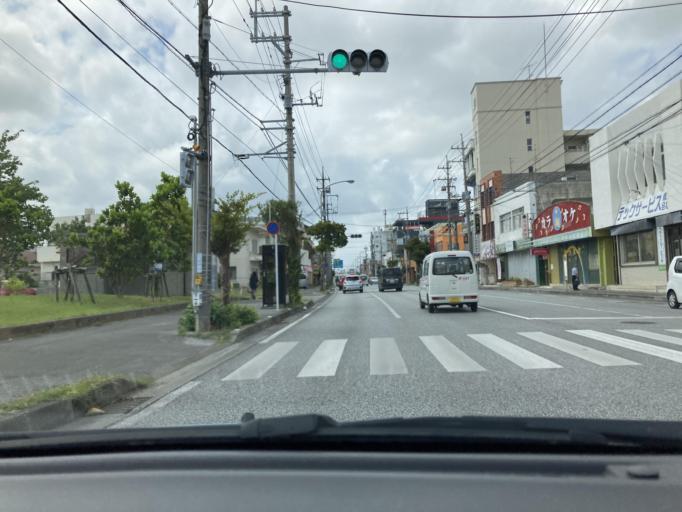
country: JP
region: Okinawa
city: Gushikawa
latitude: 26.3565
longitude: 127.8342
